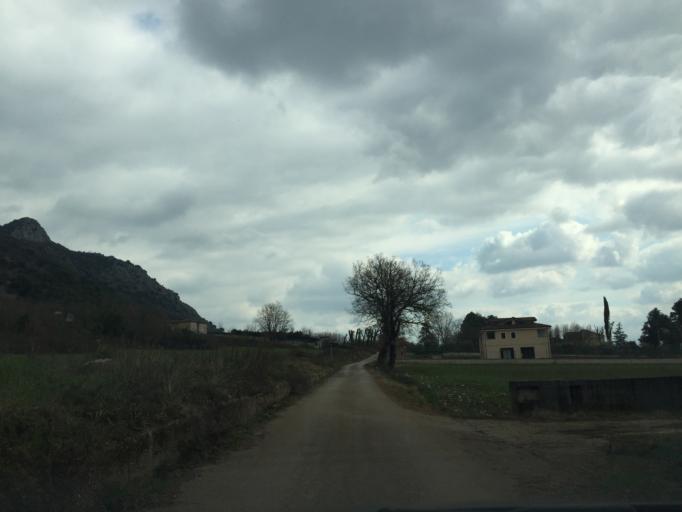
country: IT
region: Latium
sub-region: Provincia di Frosinone
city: Villa Santa Lucia
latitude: 41.4877
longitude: 13.7905
